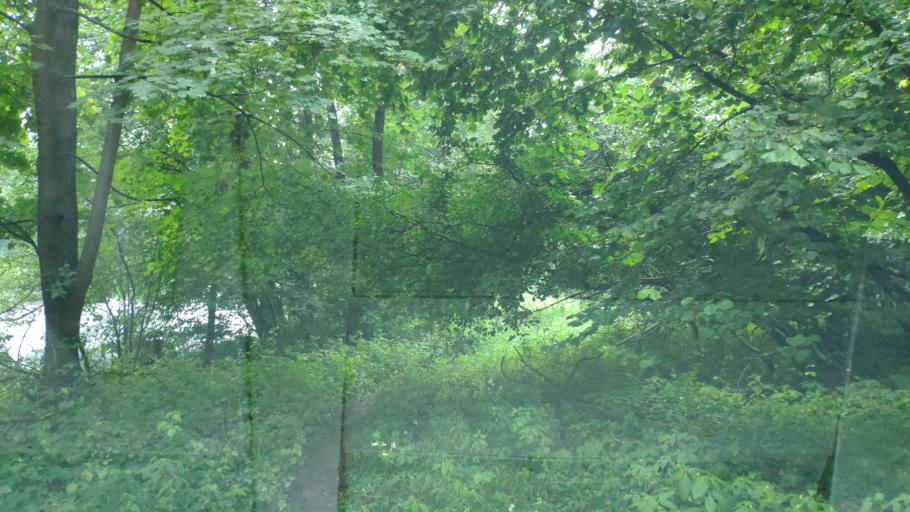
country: SK
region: Presovsky
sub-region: Okres Presov
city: Presov
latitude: 48.8674
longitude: 21.2043
